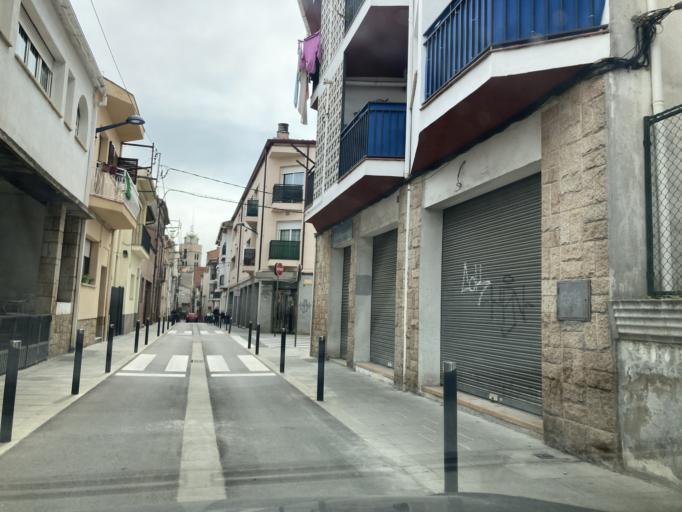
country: ES
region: Catalonia
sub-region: Provincia de Girona
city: Santa Coloma de Farners
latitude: 41.8647
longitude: 2.6606
